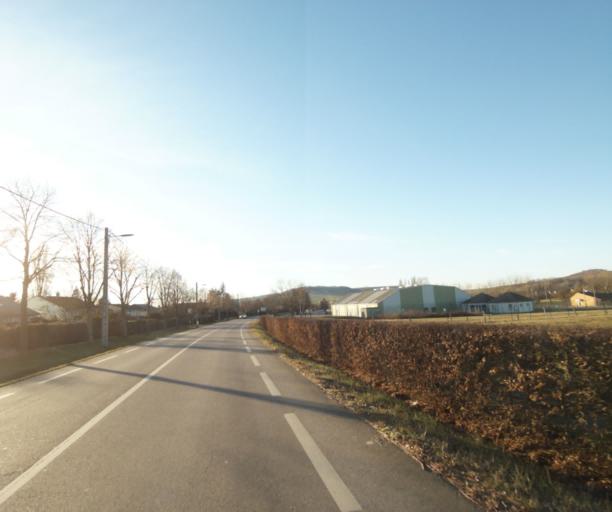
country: FR
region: Lorraine
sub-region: Departement de Meurthe-et-Moselle
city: Seichamps
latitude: 48.7042
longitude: 6.2665
